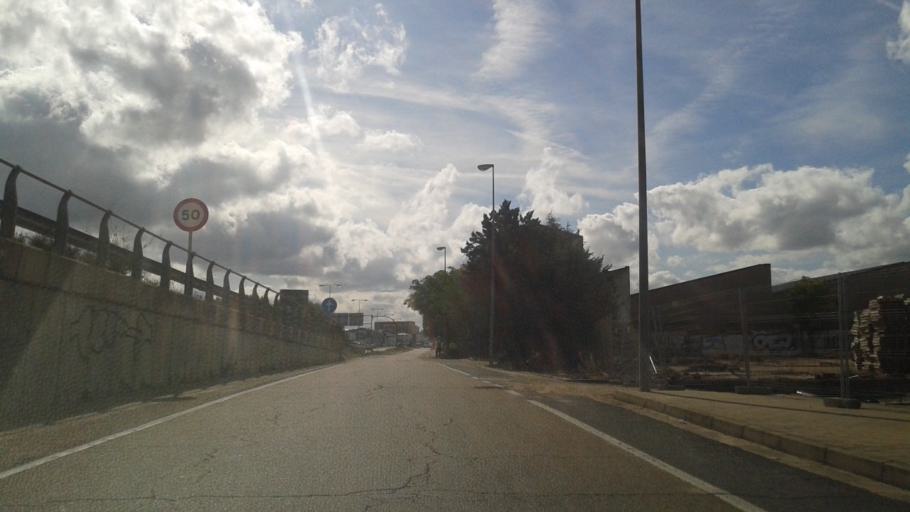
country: ES
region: Castille and Leon
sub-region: Provincia de Valladolid
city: Valladolid
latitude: 41.6776
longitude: -4.7224
